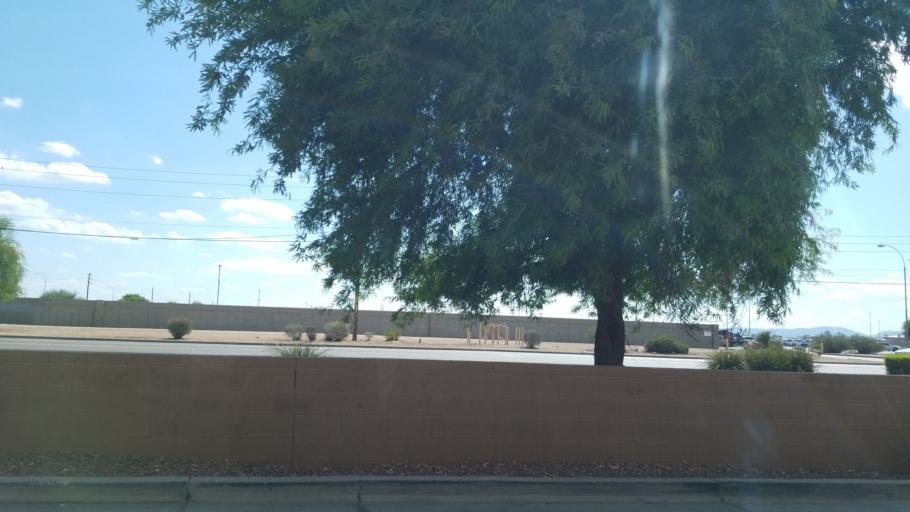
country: US
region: Arizona
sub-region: Maricopa County
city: Tolleson
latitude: 33.4512
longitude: -112.2387
